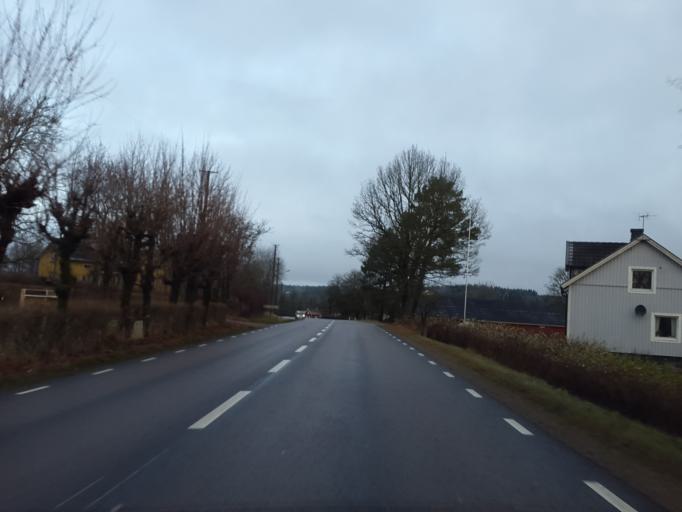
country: SE
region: Vaestra Goetaland
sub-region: Boras Kommun
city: Sandared
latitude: 57.8054
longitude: 12.7543
